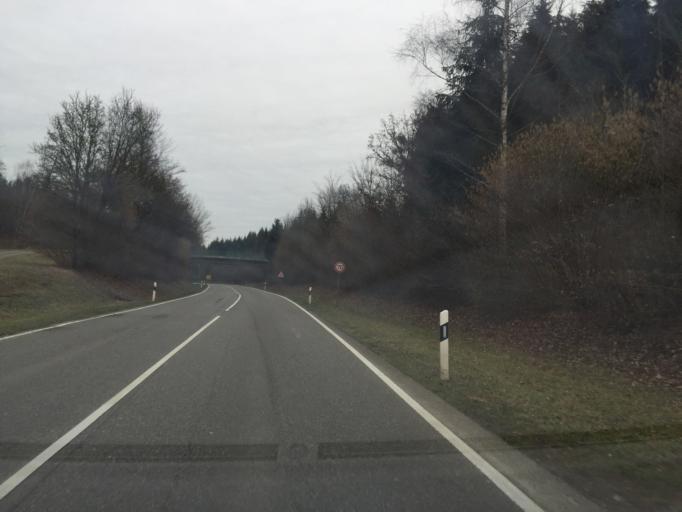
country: DE
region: Baden-Wuerttemberg
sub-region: Freiburg Region
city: Gottmadingen
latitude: 47.7372
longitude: 8.7450
